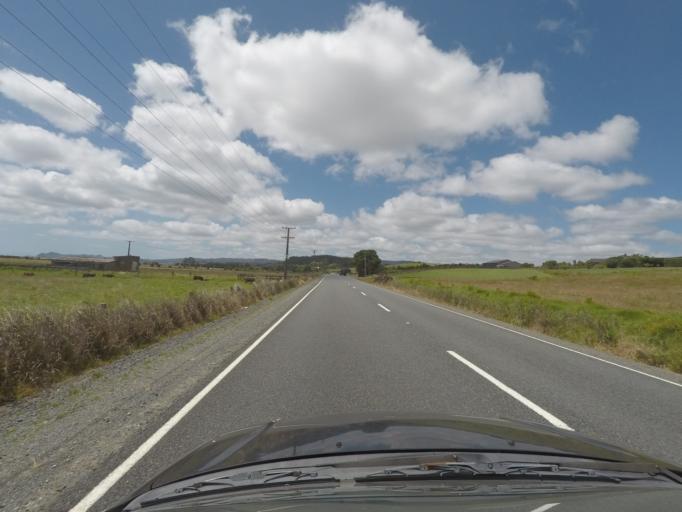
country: NZ
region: Northland
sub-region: Whangarei
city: Ruakaka
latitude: -36.0087
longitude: 174.4805
